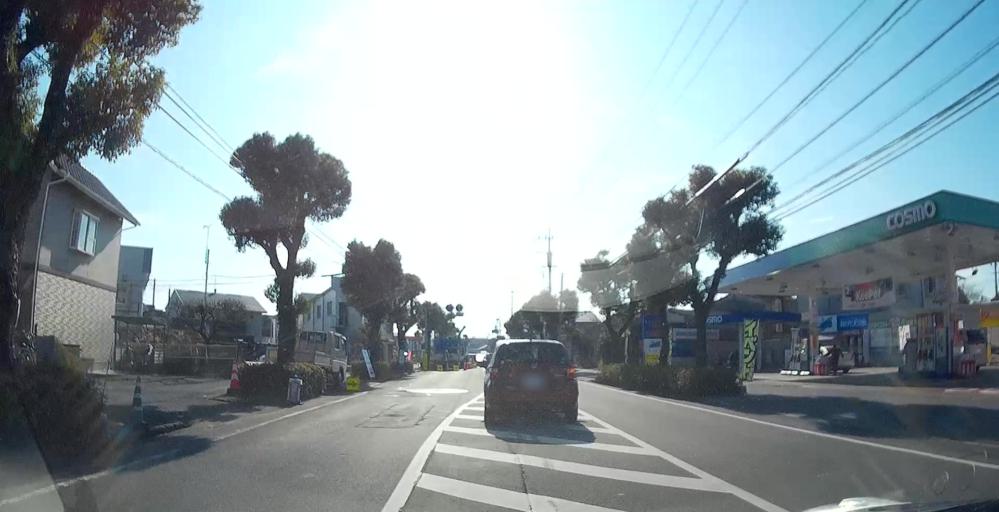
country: JP
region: Kumamoto
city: Kumamoto
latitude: 32.7479
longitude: 130.6839
